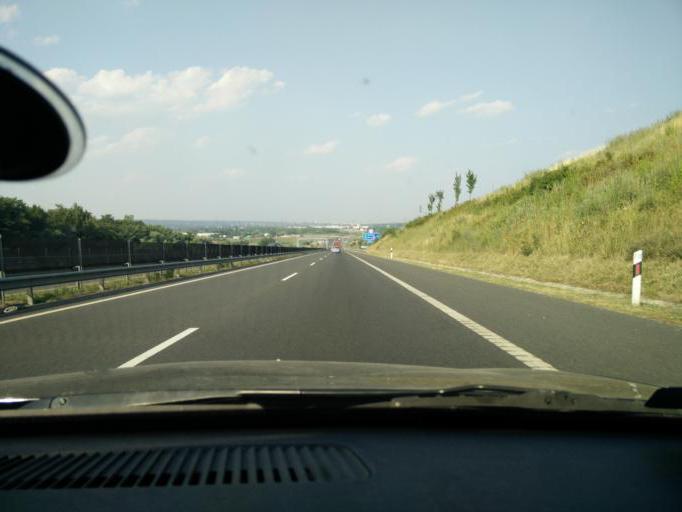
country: HU
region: Pest
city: Erd
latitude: 47.3642
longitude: 18.9219
